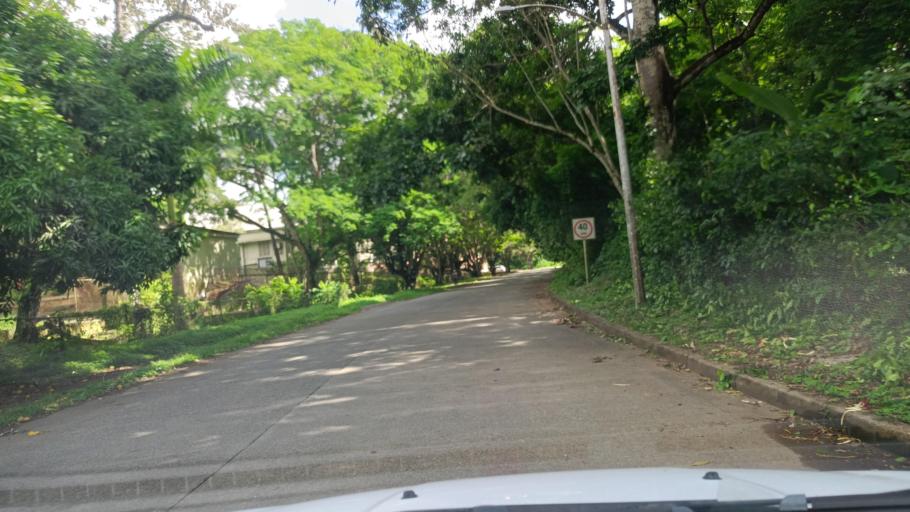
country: PA
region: Panama
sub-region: Distrito de Panama
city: Paraiso
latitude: 9.0289
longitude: -79.6258
